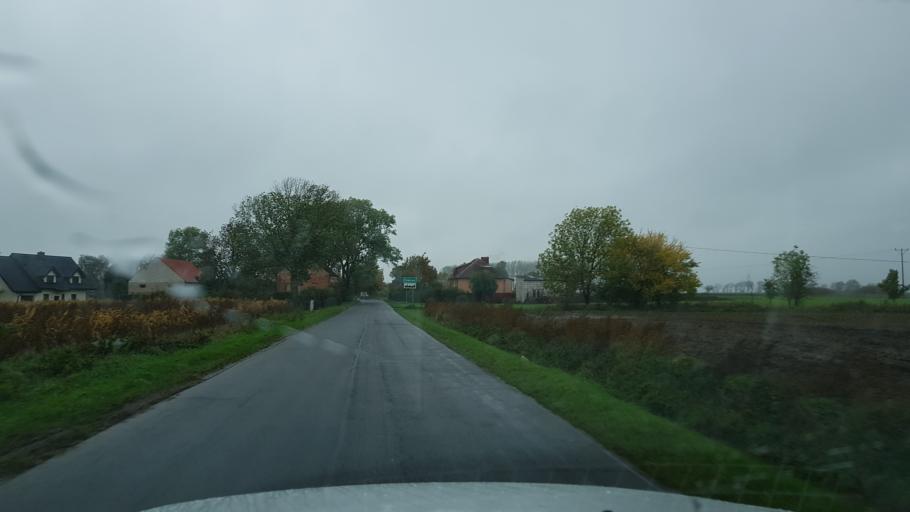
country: PL
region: West Pomeranian Voivodeship
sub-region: Powiat pyrzycki
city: Pyrzyce
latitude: 53.1588
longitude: 14.8506
